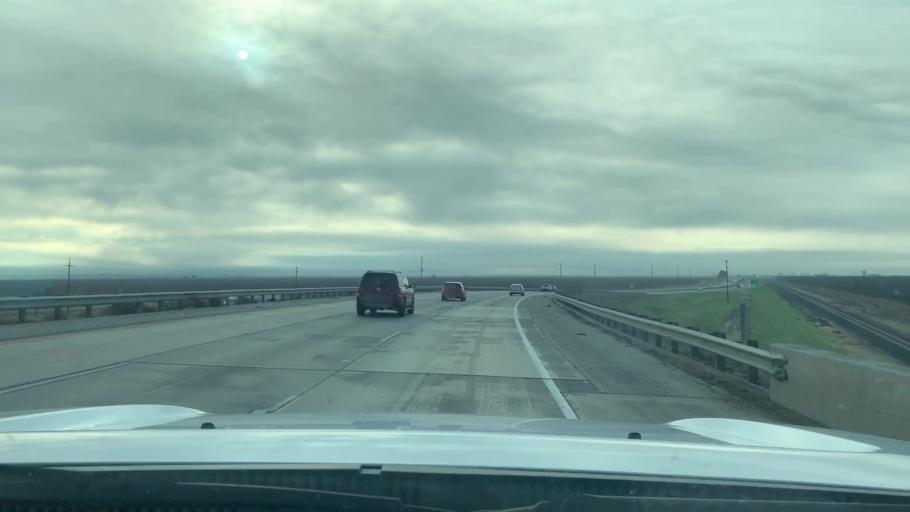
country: US
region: California
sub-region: Kern County
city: McFarland
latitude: 35.5902
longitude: -119.2058
